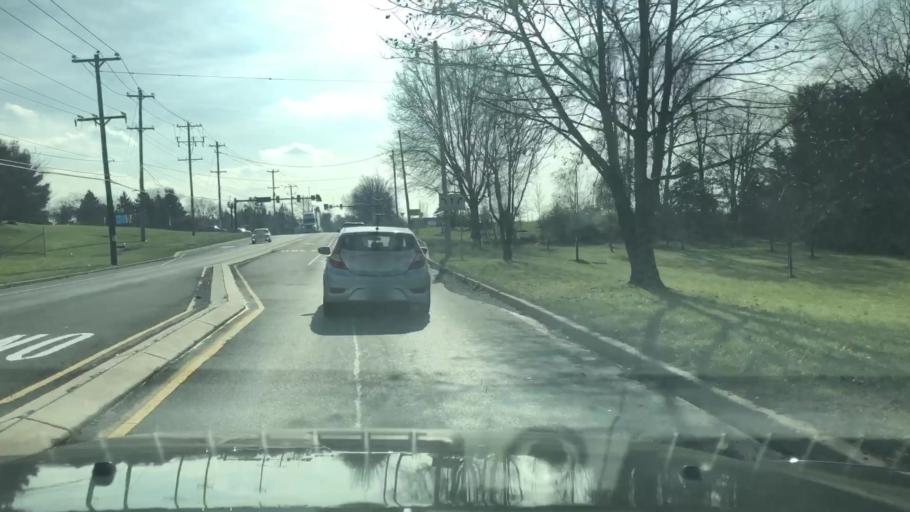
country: US
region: Pennsylvania
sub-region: Bucks County
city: Newtown
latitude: 40.2030
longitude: -74.9298
